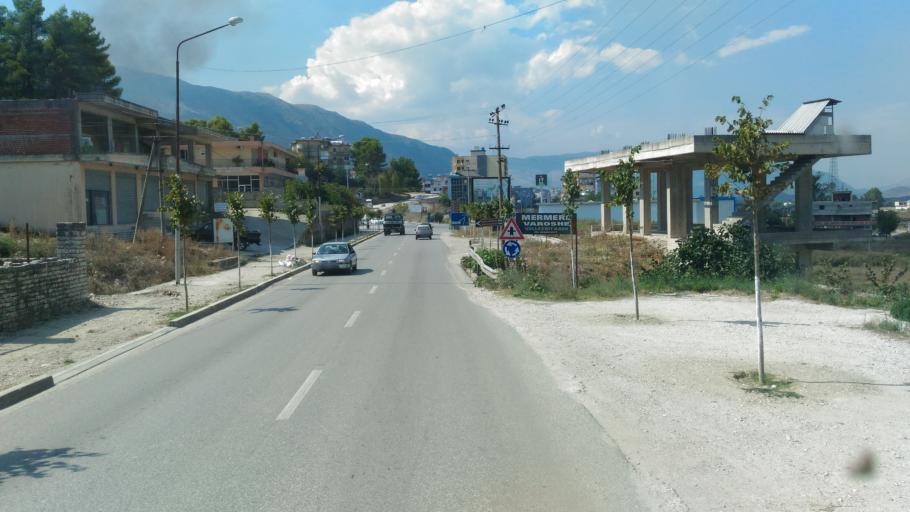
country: AL
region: Gjirokaster
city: Gjirokaster
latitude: 40.0765
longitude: 20.1526
